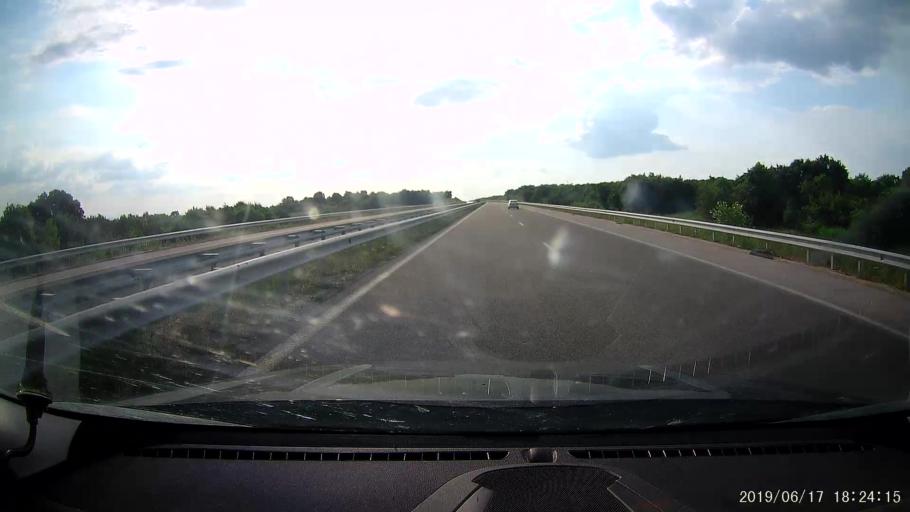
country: BG
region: Khaskovo
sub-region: Obshtina Dimitrovgrad
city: Dimitrovgrad
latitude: 41.9825
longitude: 25.6968
